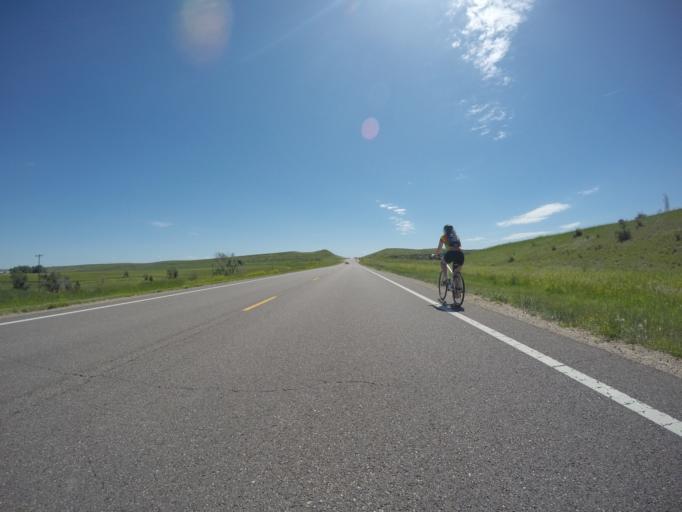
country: US
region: Kansas
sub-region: Rawlins County
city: Atwood
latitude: 39.8134
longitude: -101.0036
